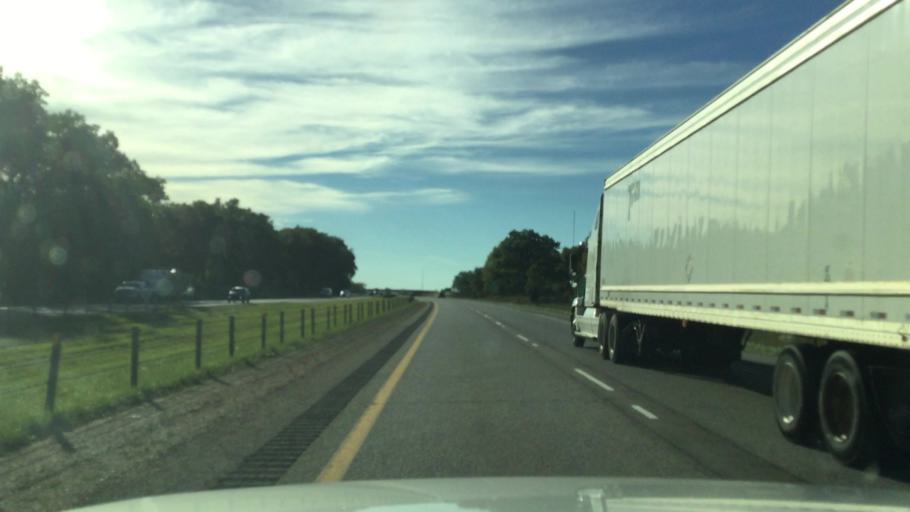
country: US
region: Michigan
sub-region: Kalamazoo County
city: Galesburg
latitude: 42.2824
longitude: -85.3647
